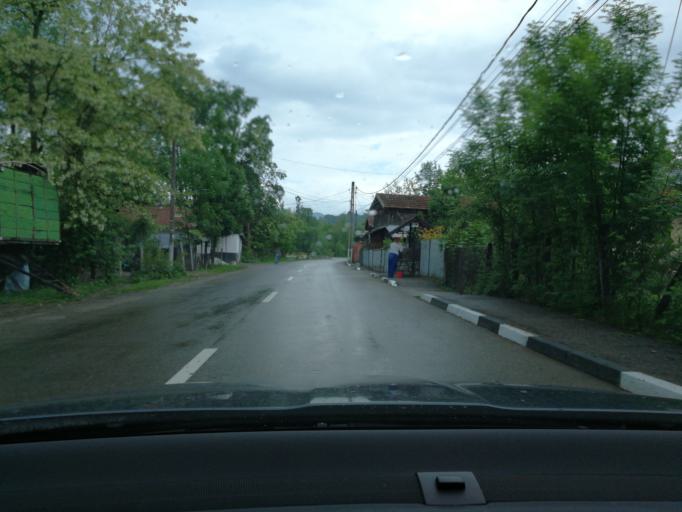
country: RO
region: Prahova
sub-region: Comuna Alunis
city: Alunis
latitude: 45.2011
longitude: 25.8660
